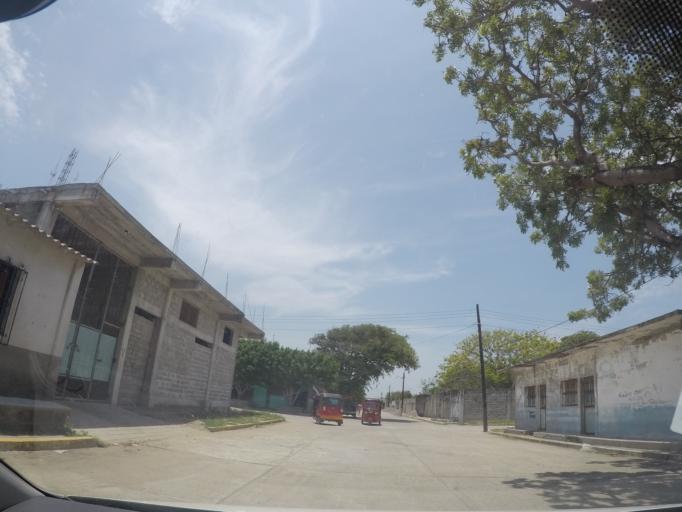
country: MX
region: Oaxaca
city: San Mateo del Mar
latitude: 16.2103
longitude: -94.9805
